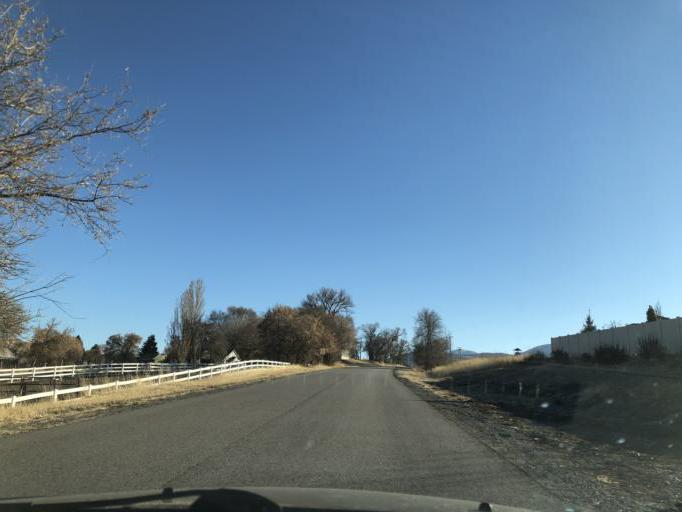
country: US
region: Utah
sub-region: Cache County
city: Wellsville
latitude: 41.6097
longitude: -111.9305
